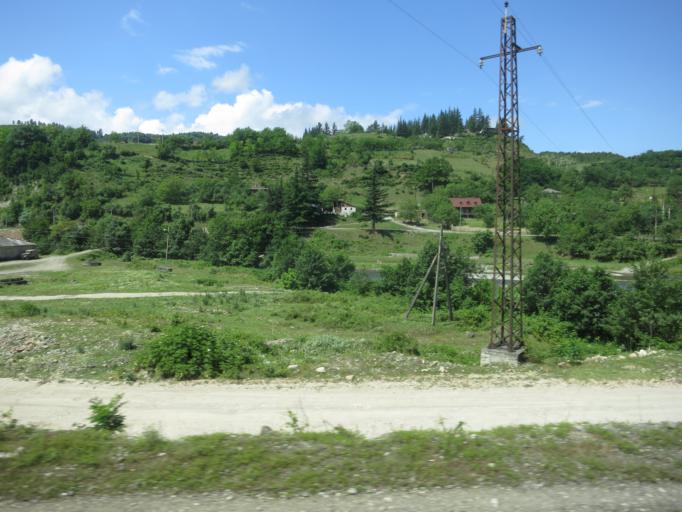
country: GE
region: Imereti
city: Kharagauli
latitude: 42.0256
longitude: 43.1991
